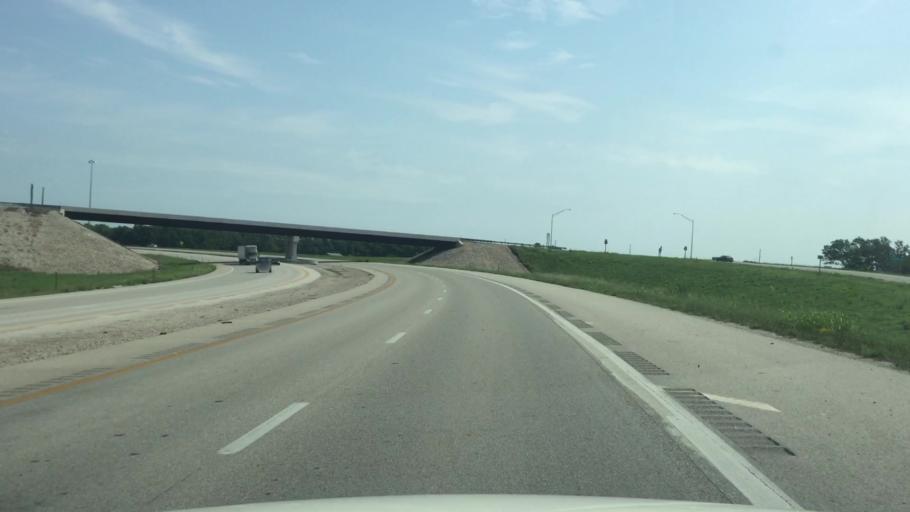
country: US
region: Kansas
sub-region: Montgomery County
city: Coffeyville
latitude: 37.0447
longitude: -95.5835
